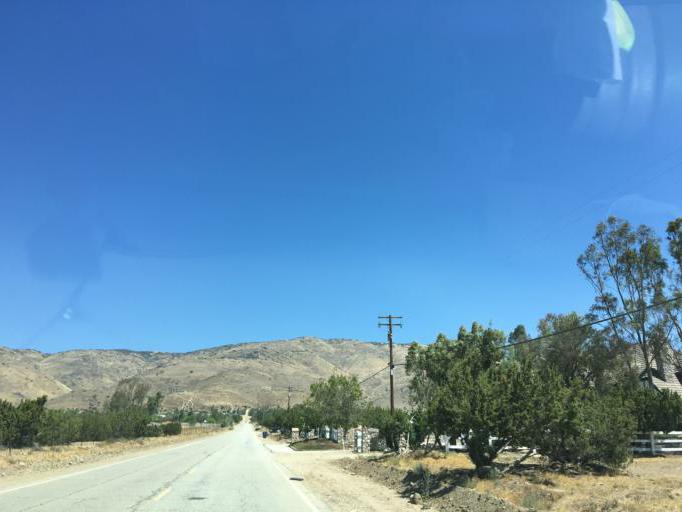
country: US
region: California
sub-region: Los Angeles County
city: Acton
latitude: 34.5177
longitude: -118.2380
